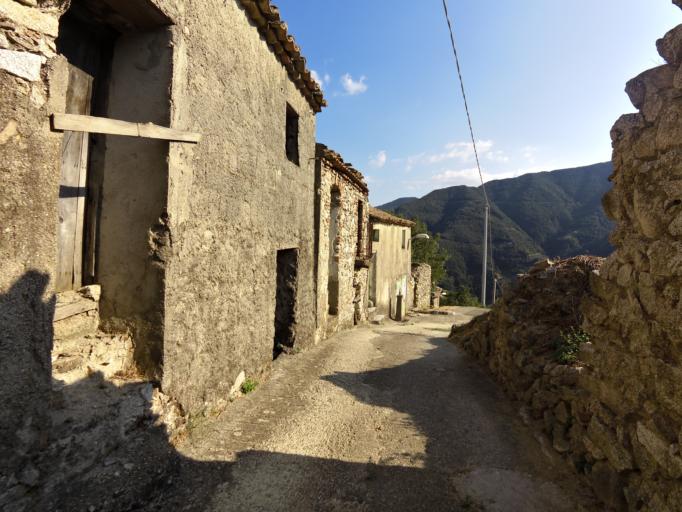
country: IT
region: Calabria
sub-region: Provincia di Vibo-Valentia
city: Nardodipace
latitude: 38.4476
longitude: 16.3472
